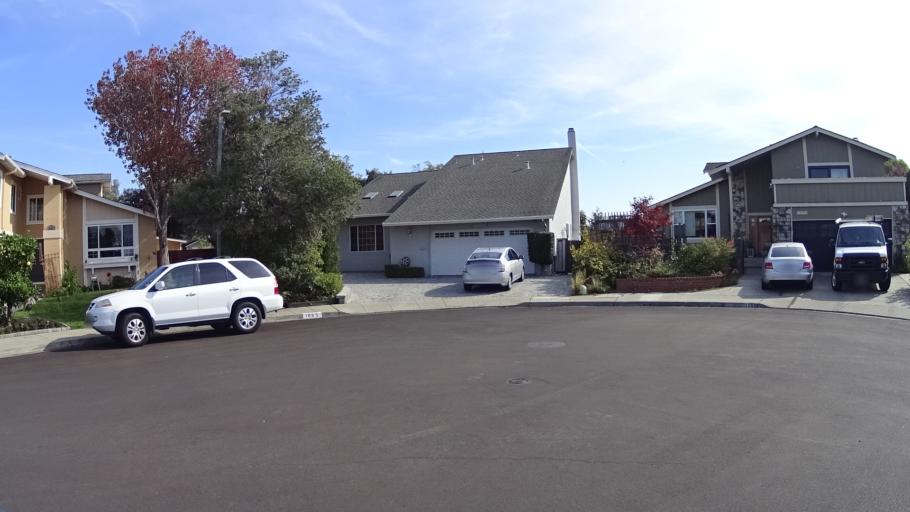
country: US
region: California
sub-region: San Mateo County
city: Foster City
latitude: 37.5406
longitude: -122.2744
